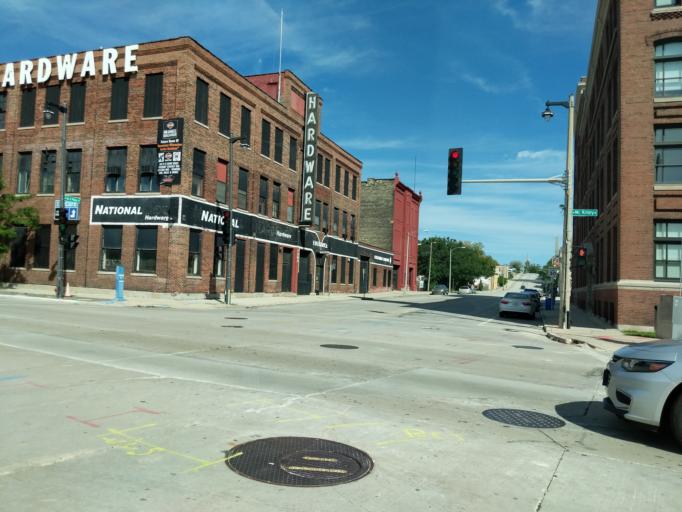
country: US
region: Wisconsin
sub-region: Milwaukee County
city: Milwaukee
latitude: 43.0470
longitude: -87.9158
